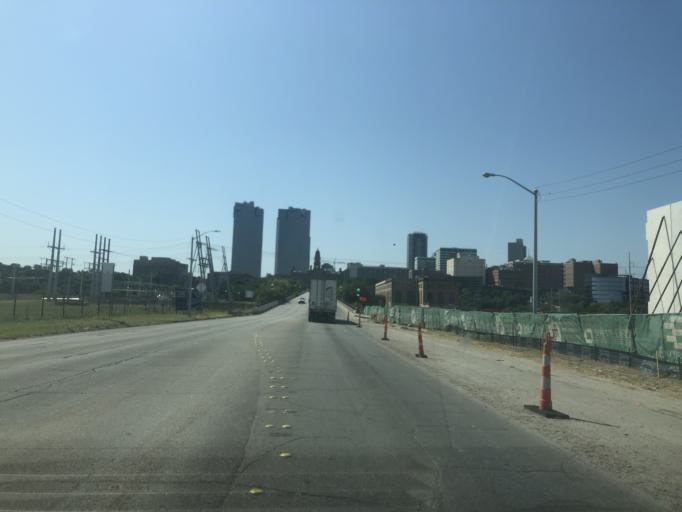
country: US
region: Texas
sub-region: Tarrant County
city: Fort Worth
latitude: 32.7635
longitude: -97.3373
